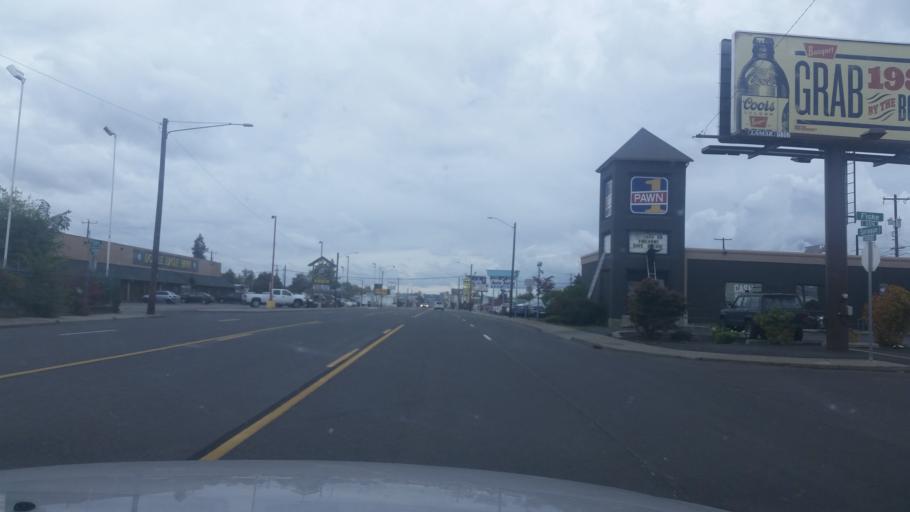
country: US
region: Washington
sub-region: Spokane County
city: Spokane
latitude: 47.6574
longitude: -117.3650
